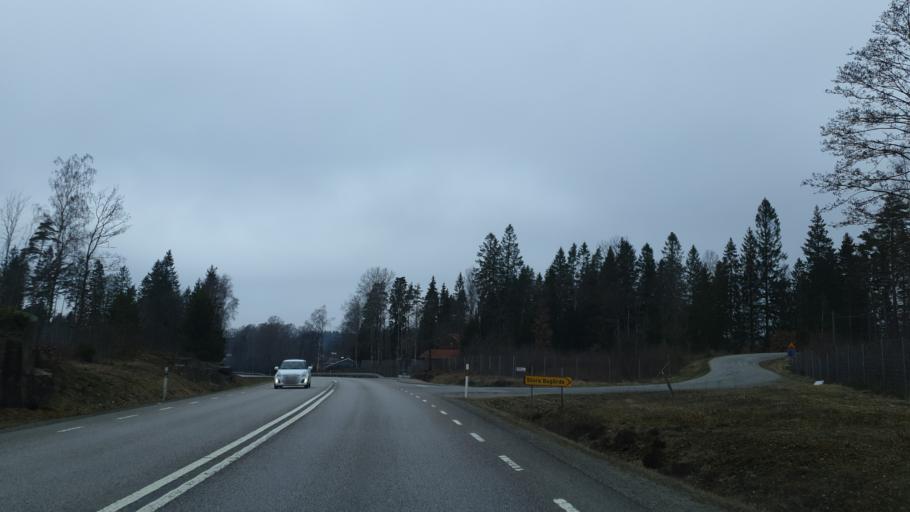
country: SE
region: Vaestra Goetaland
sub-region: Harryda Kommun
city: Hindas
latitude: 57.6525
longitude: 12.3966
